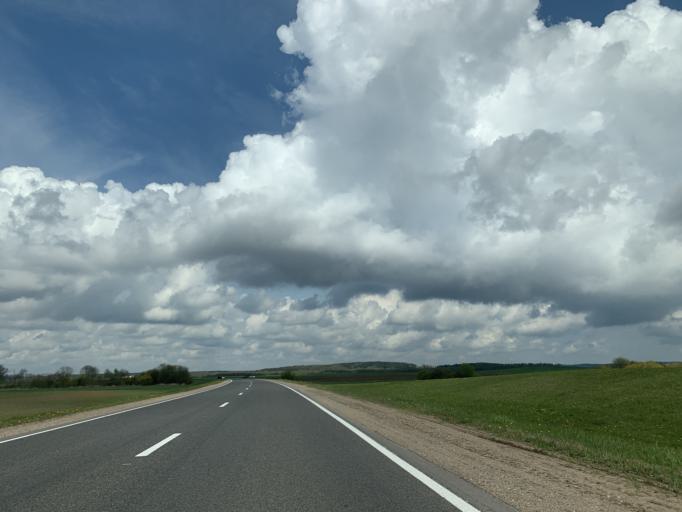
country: BY
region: Minsk
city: Nyasvizh
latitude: 53.2327
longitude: 26.7214
